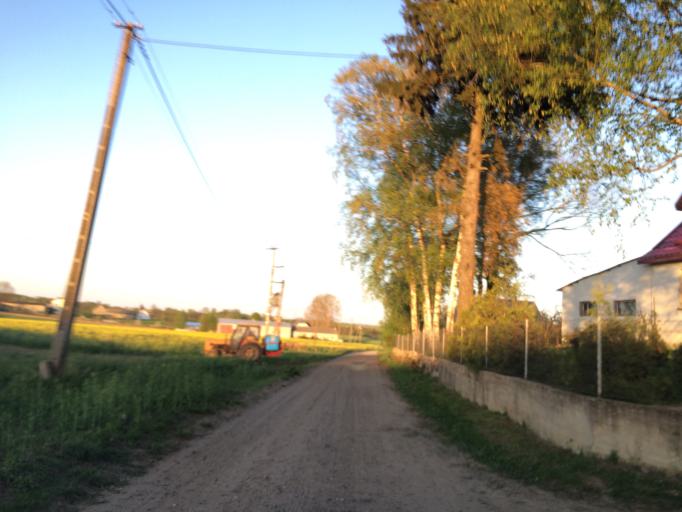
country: PL
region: Warmian-Masurian Voivodeship
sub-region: Powiat dzialdowski
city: Rybno
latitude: 53.4710
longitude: 19.9068
